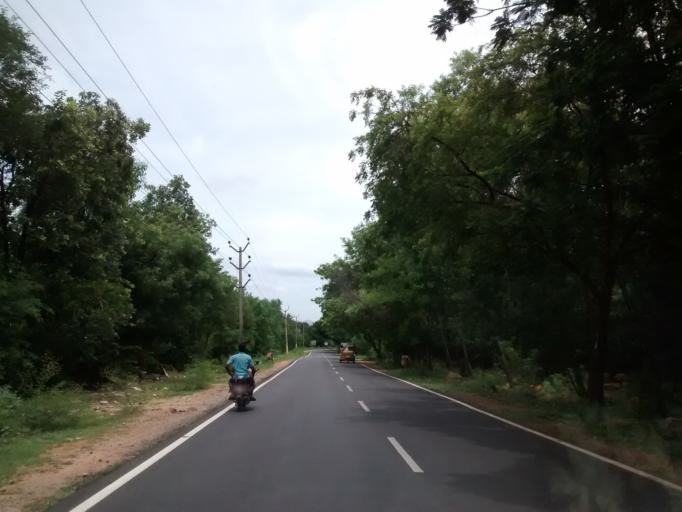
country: IN
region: Andhra Pradesh
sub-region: Chittoor
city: Tirupati
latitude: 13.6333
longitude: 79.3884
